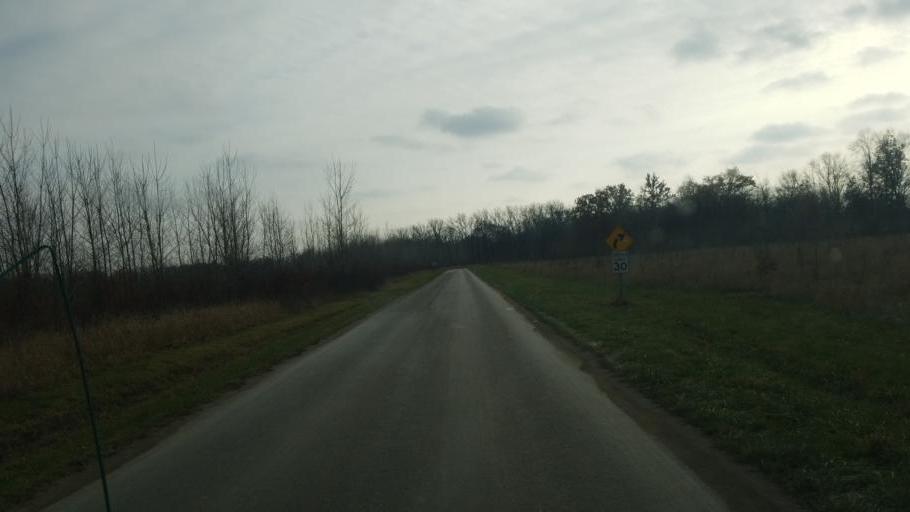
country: US
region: Indiana
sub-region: Adams County
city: Geneva
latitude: 40.6199
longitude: -84.9637
